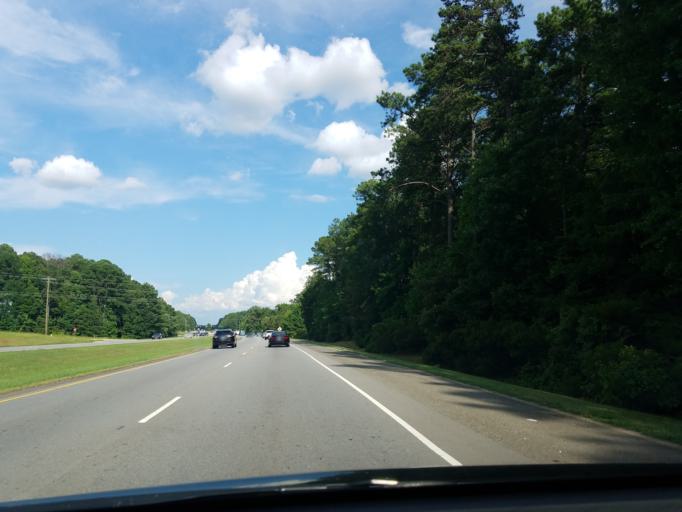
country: US
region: North Carolina
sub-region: Wake County
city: Apex
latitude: 35.7450
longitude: -78.8276
